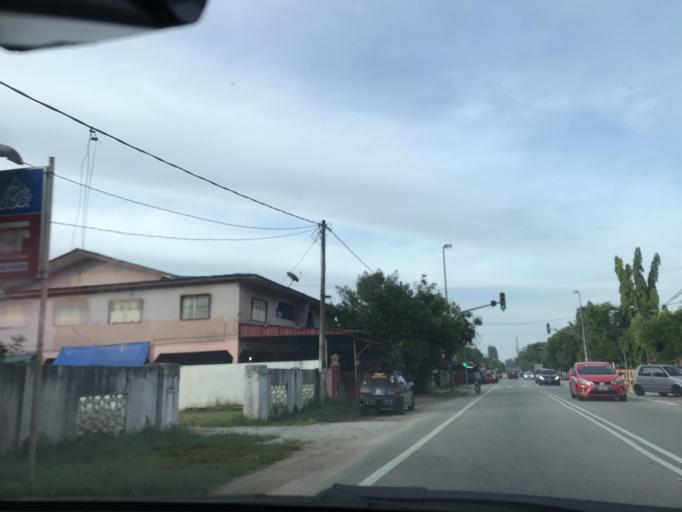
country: MY
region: Kelantan
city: Kota Bharu
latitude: 6.1004
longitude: 102.2102
